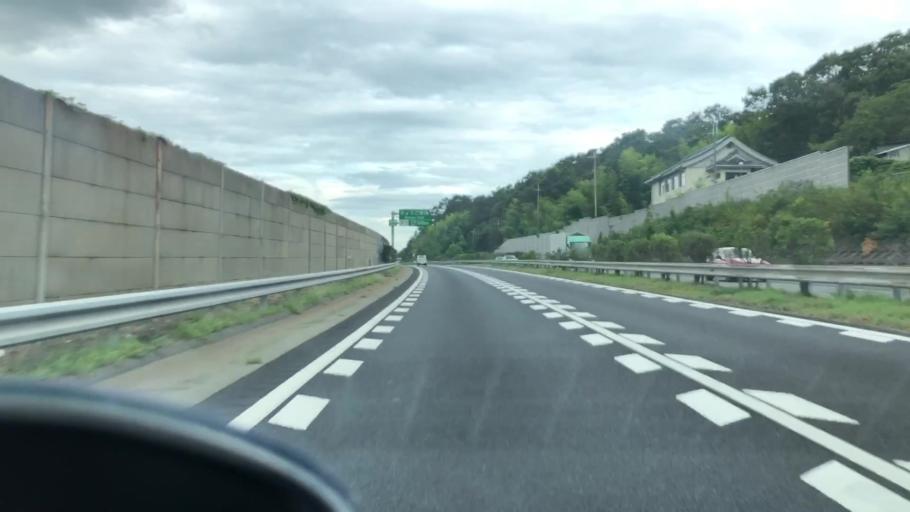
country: JP
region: Hyogo
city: Yashiro
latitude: 34.8994
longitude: 135.0716
